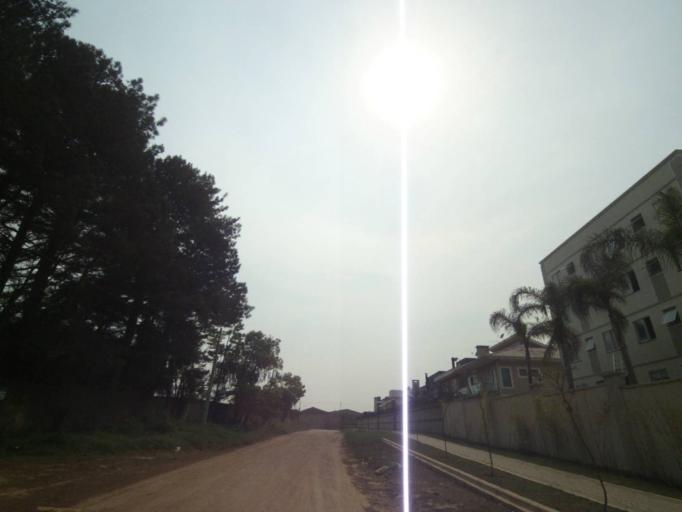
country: BR
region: Parana
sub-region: Sao Jose Dos Pinhais
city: Sao Jose dos Pinhais
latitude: -25.5144
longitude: -49.2856
